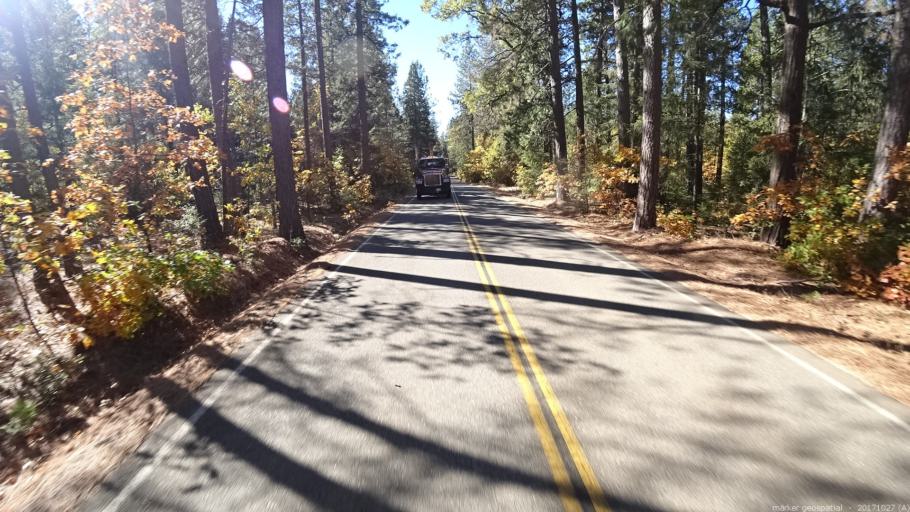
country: US
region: California
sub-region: Shasta County
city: Shingletown
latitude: 40.7112
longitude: -121.9545
